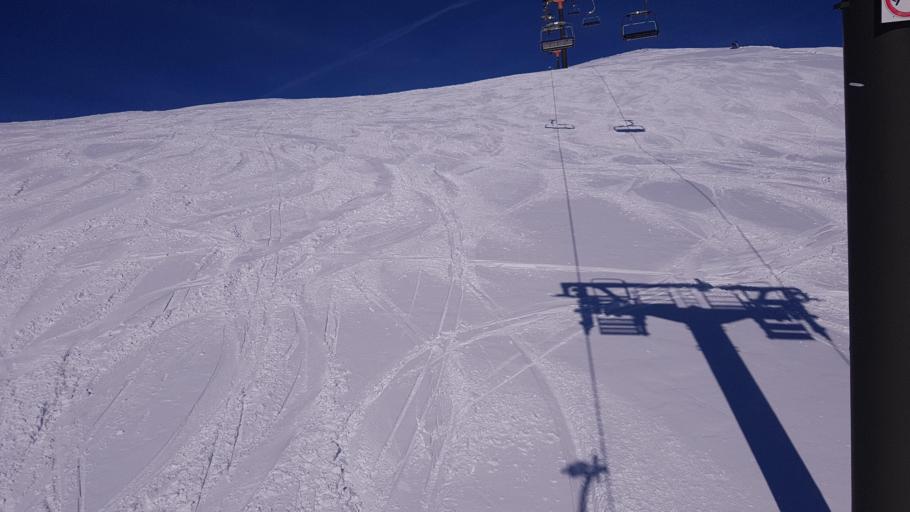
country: AT
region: Salzburg
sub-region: Politischer Bezirk Zell am See
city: Neukirchen am Grossvenediger
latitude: 47.2826
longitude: 12.2658
